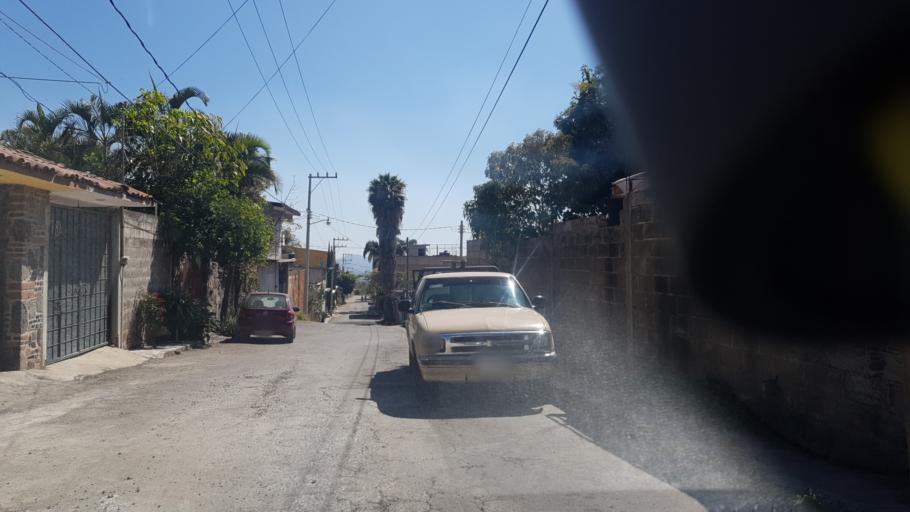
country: MX
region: Morelos
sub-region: Cuernavaca
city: Villa Santiago
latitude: 18.9736
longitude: -99.1833
